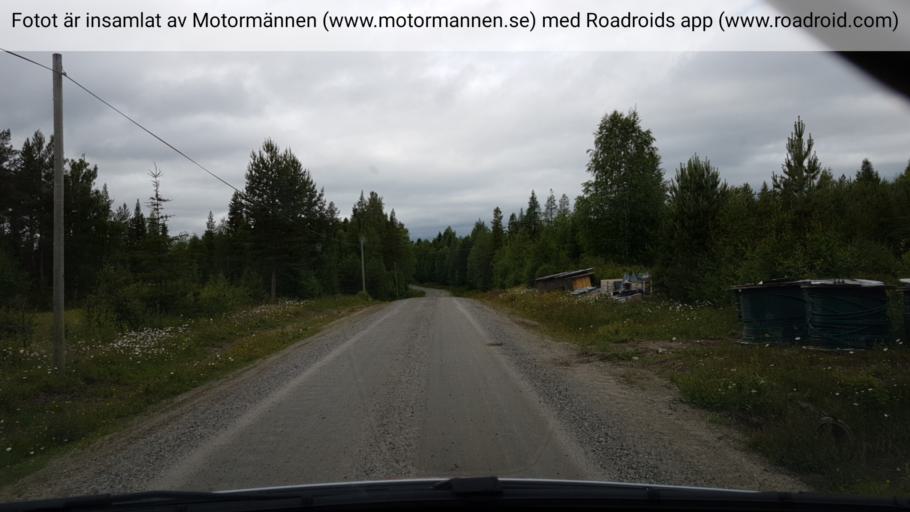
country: SE
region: Vaesterbotten
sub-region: Lycksele Kommun
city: Lycksele
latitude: 64.5716
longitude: 19.0133
